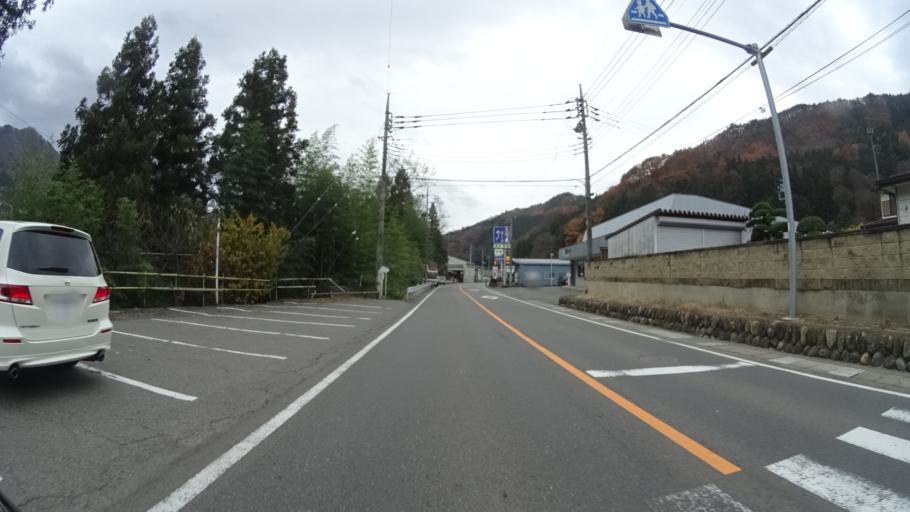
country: JP
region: Gunma
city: Numata
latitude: 36.6932
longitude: 139.2092
